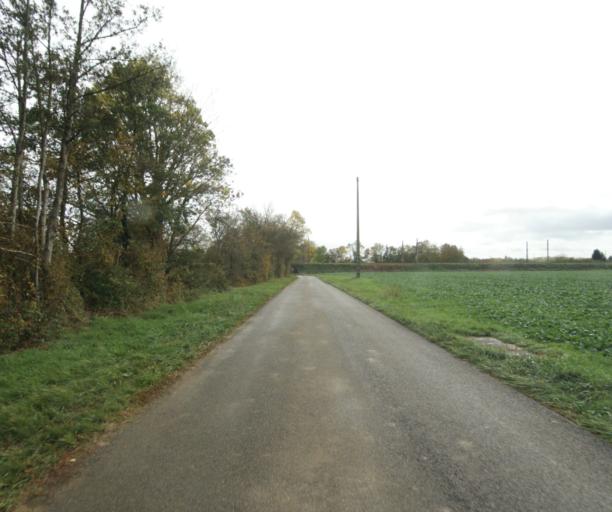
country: FR
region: Rhone-Alpes
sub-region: Departement de l'Ain
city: Pont-de-Vaux
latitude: 46.4706
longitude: 4.8931
